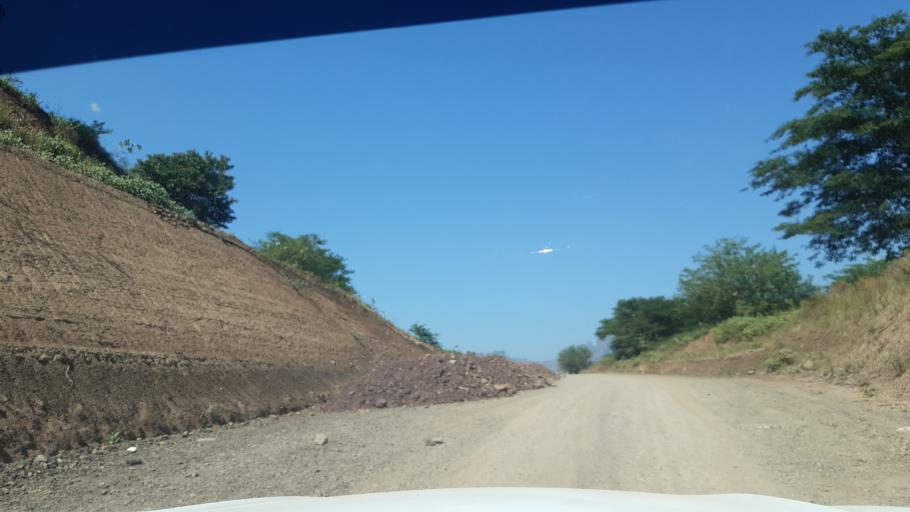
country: ET
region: Amhara
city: Dabat
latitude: 13.1929
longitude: 37.5705
